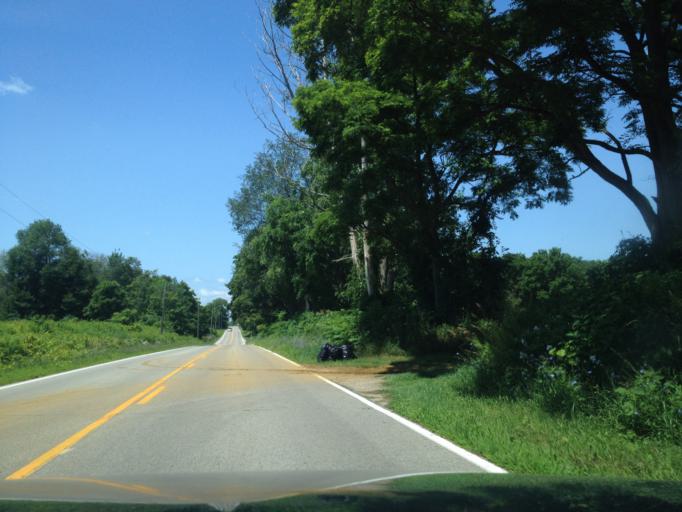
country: CA
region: Ontario
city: Aylmer
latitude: 42.6199
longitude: -80.7134
